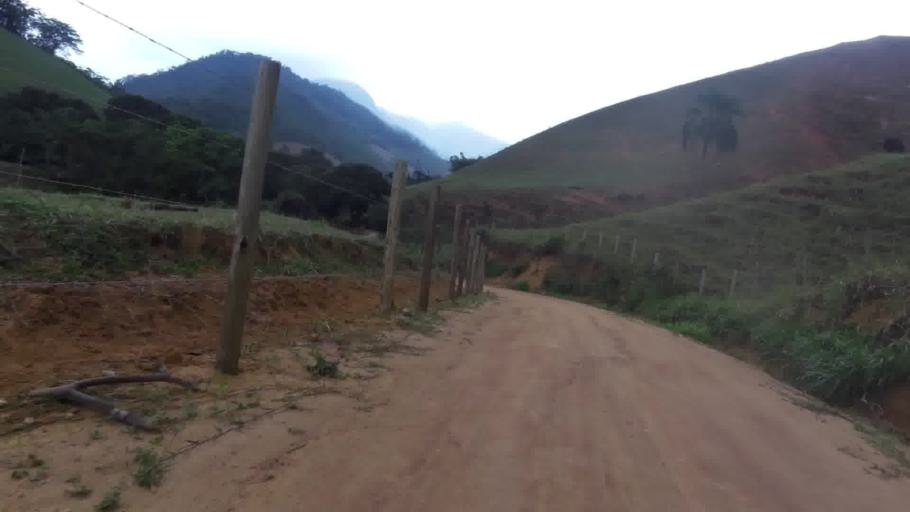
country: BR
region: Espirito Santo
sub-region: Alfredo Chaves
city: Alfredo Chaves
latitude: -20.6272
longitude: -40.7522
